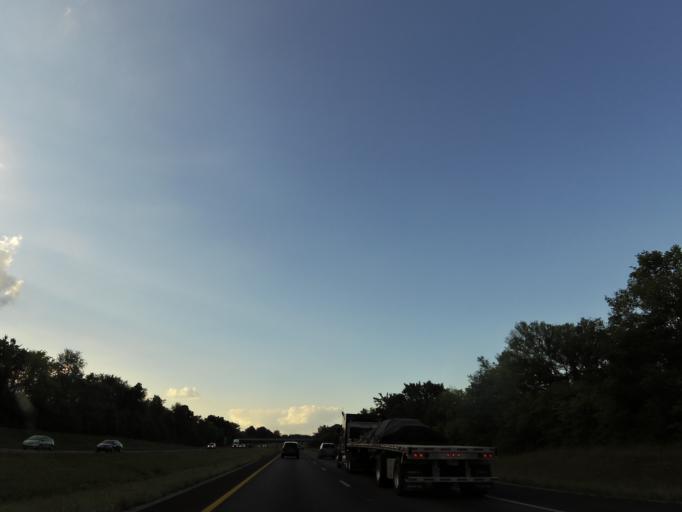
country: US
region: Tennessee
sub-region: Williamson County
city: Thompson's Station
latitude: 35.7858
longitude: -86.8619
